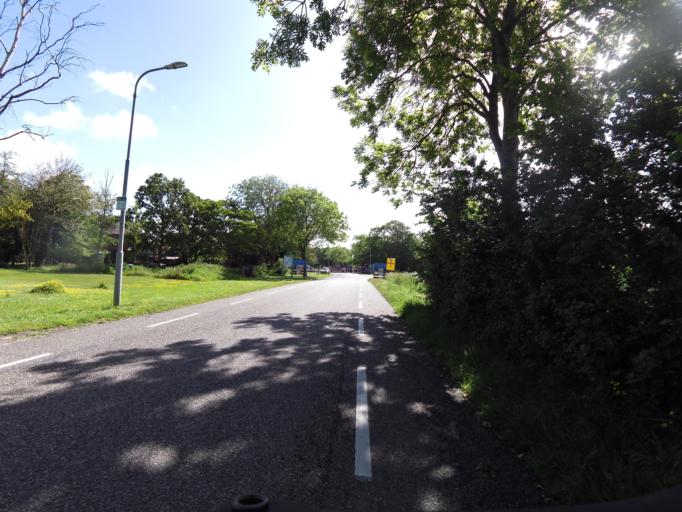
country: NL
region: Zeeland
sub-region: Schouwen-Duiveland
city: Scharendijke
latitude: 51.6934
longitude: 3.9310
